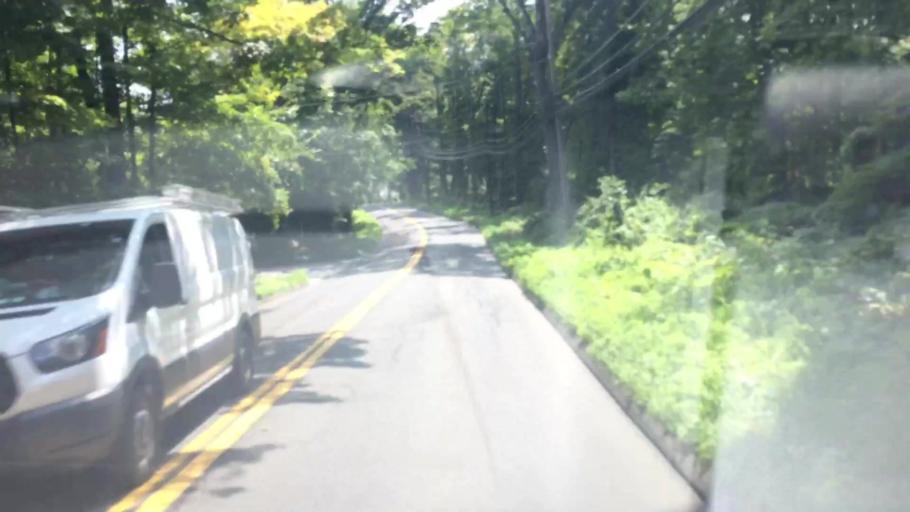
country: US
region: Connecticut
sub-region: Fairfield County
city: Danbury
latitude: 41.4036
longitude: -73.4760
